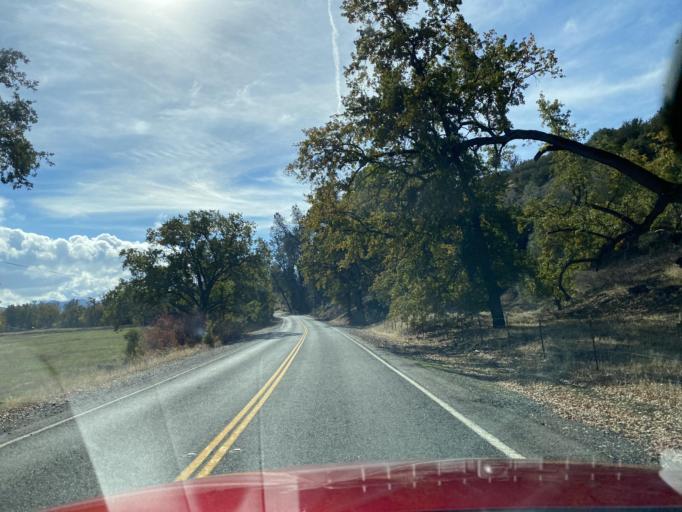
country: US
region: California
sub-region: Glenn County
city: Willows
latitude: 39.4465
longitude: -122.5136
